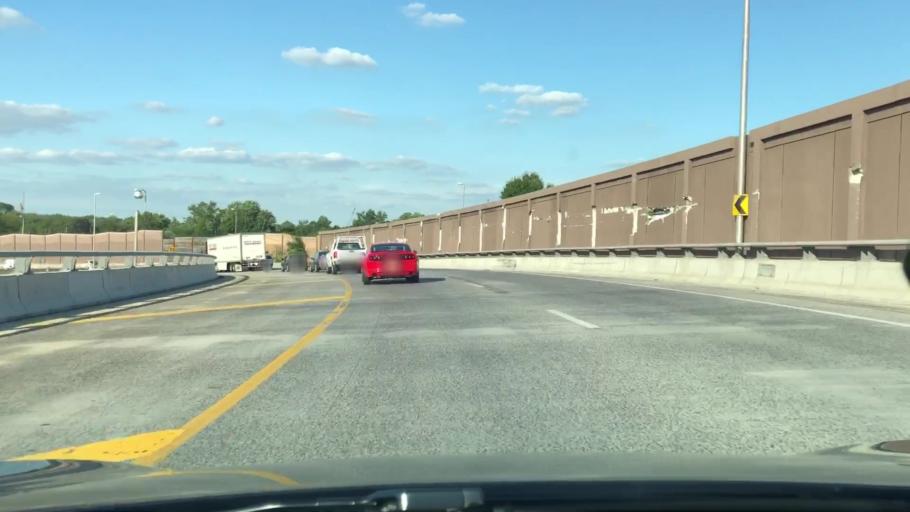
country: US
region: New Jersey
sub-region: Camden County
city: Bellmawr
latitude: 39.8673
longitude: -75.1010
